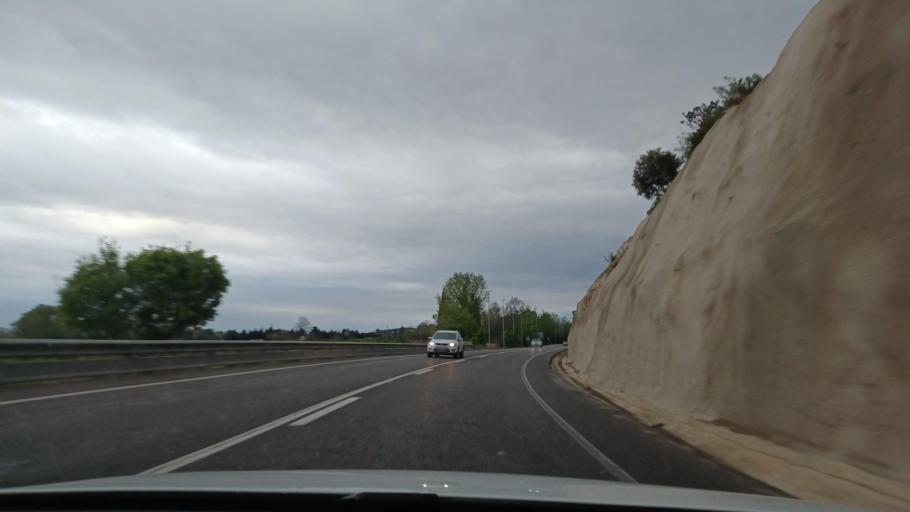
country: ES
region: Catalonia
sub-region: Provincia de Tarragona
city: Tortosa
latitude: 40.7859
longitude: 0.5013
